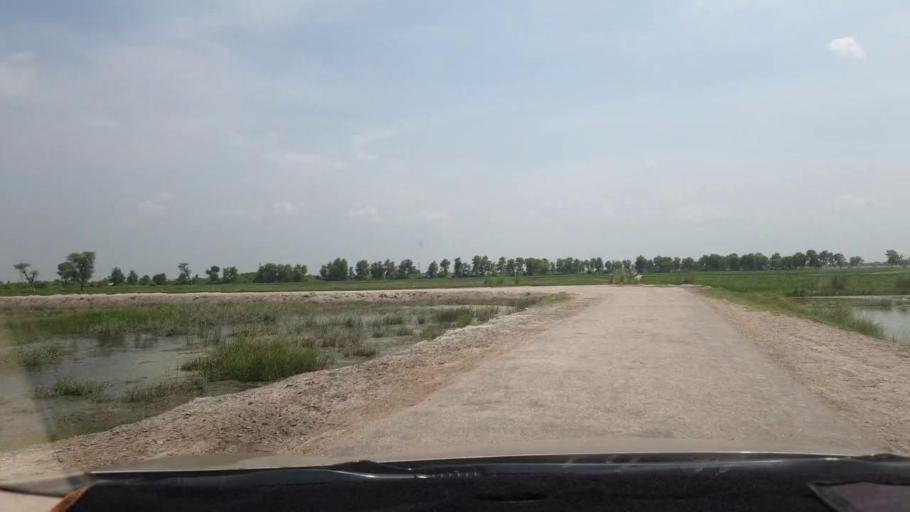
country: PK
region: Sindh
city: Naudero
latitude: 27.7335
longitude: 68.3325
